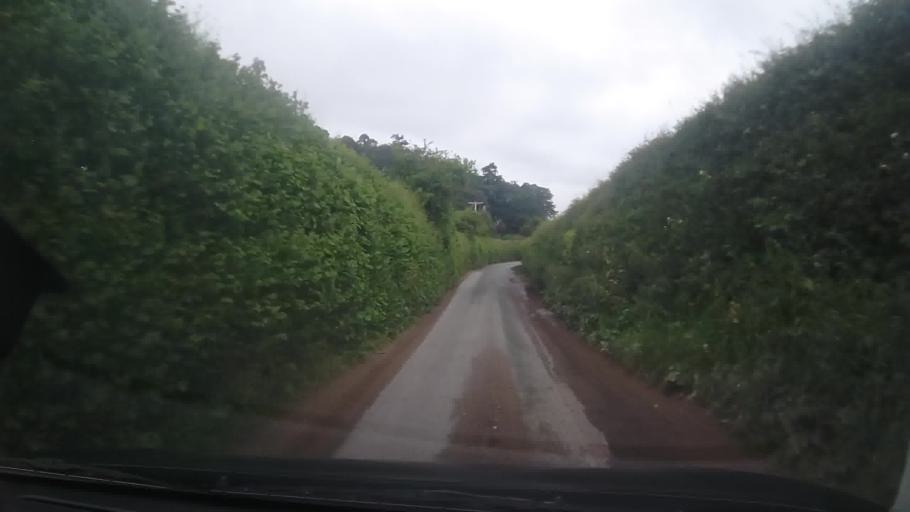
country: GB
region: England
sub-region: Shropshire
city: Clive
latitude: 52.7778
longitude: -2.7623
